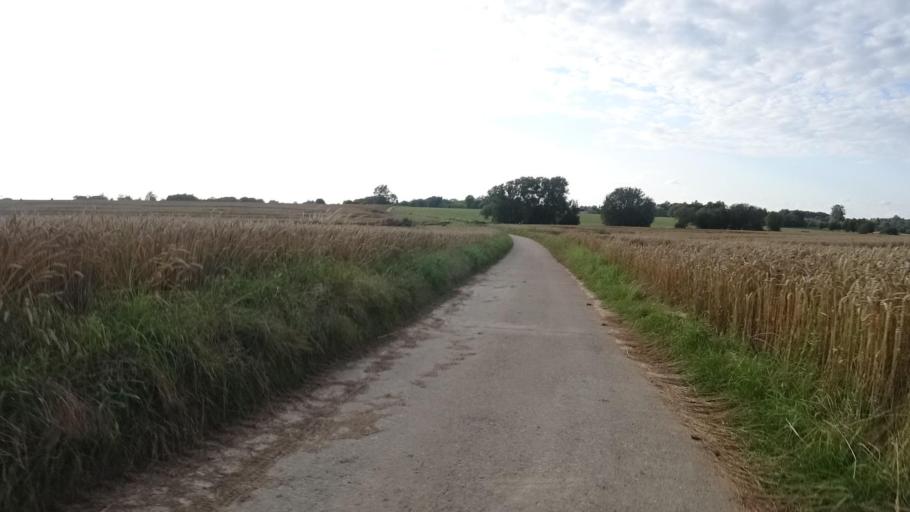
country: BE
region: Wallonia
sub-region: Province du Brabant Wallon
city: Walhain-Saint-Paul
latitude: 50.6369
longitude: 4.6874
